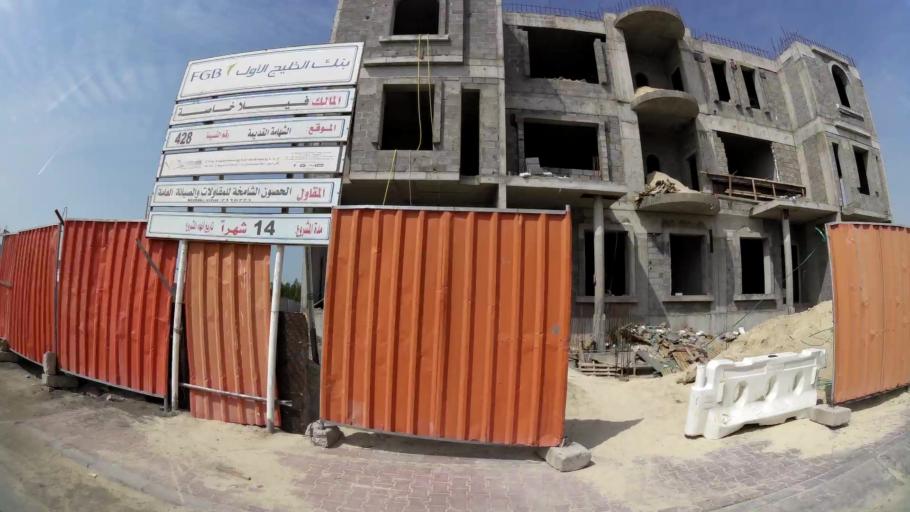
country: AE
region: Abu Dhabi
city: Abu Dhabi
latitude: 24.5451
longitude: 54.6777
